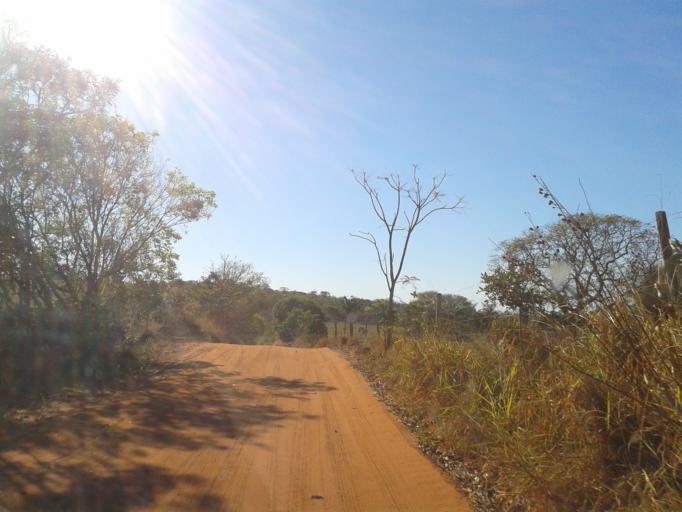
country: BR
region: Minas Gerais
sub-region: Ituiutaba
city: Ituiutaba
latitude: -19.0618
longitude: -49.3549
